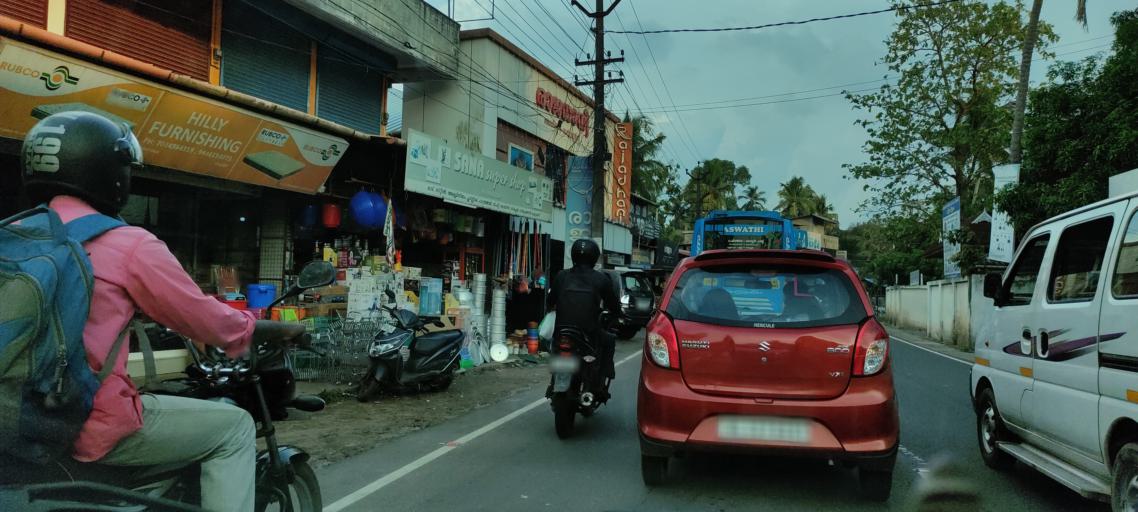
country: IN
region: Kerala
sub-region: Alappuzha
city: Arukutti
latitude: 9.8501
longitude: 76.3281
